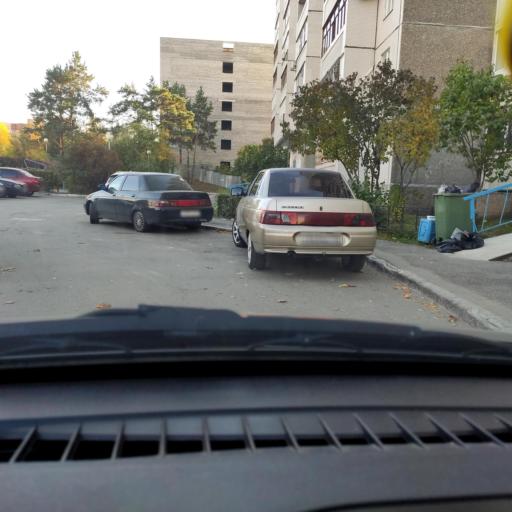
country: RU
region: Samara
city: Tol'yatti
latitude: 53.5386
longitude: 49.3524
